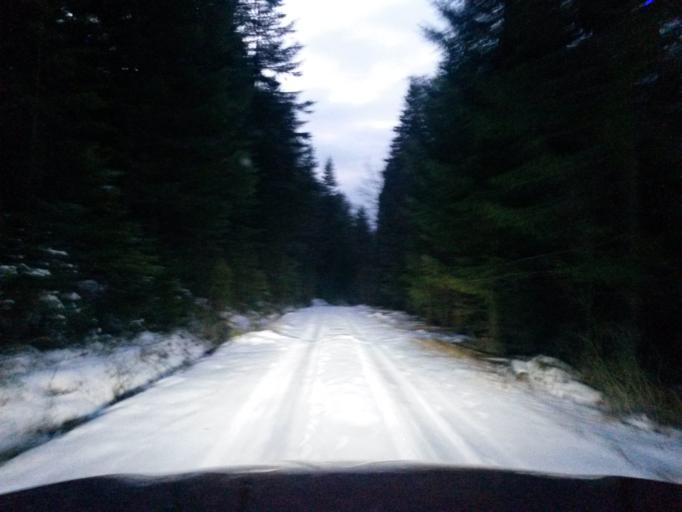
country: SK
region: Kosicky
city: Medzev
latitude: 48.7836
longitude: 20.8135
